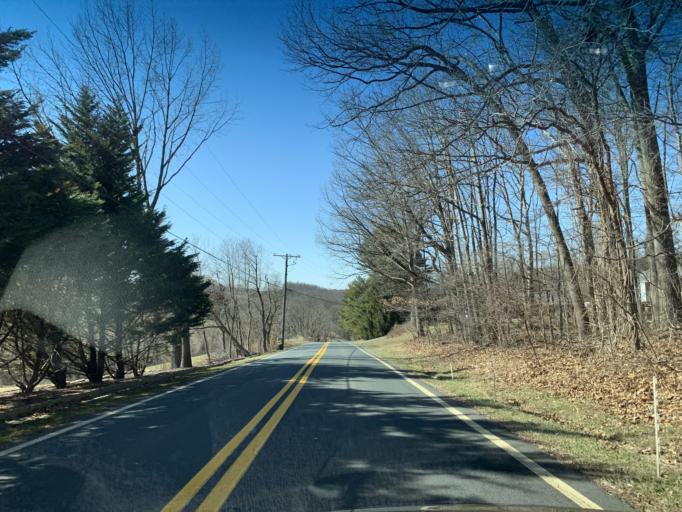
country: US
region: Maryland
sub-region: Carroll County
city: Hampstead
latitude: 39.5732
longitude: -76.8812
